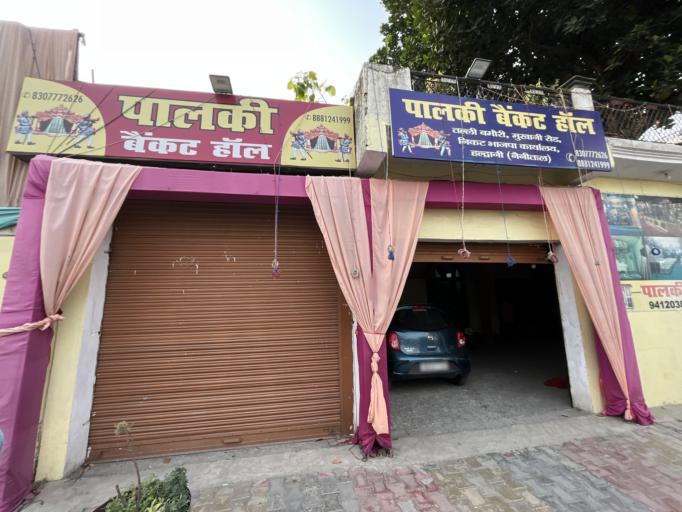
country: IN
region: Uttarakhand
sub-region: Naini Tal
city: Haldwani
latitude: 29.2219
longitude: 79.5209
